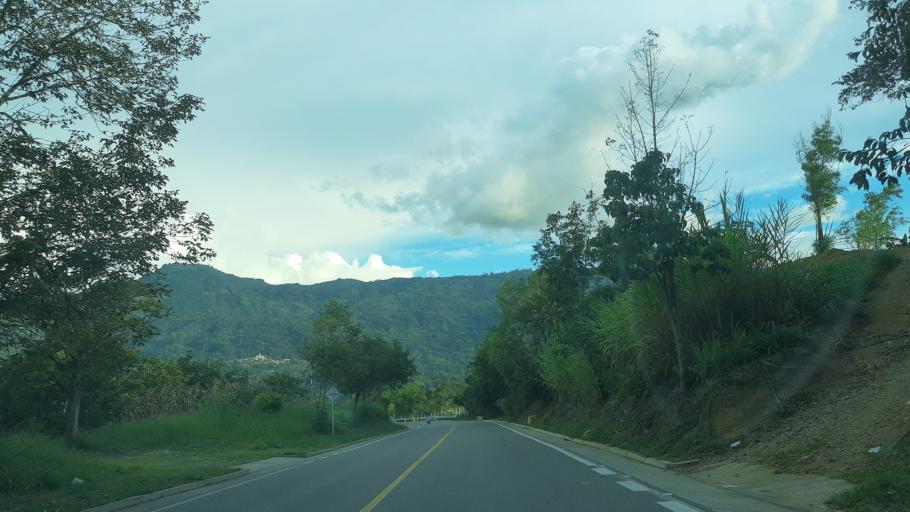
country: CO
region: Boyaca
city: Guateque
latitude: 5.0078
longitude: -73.4534
